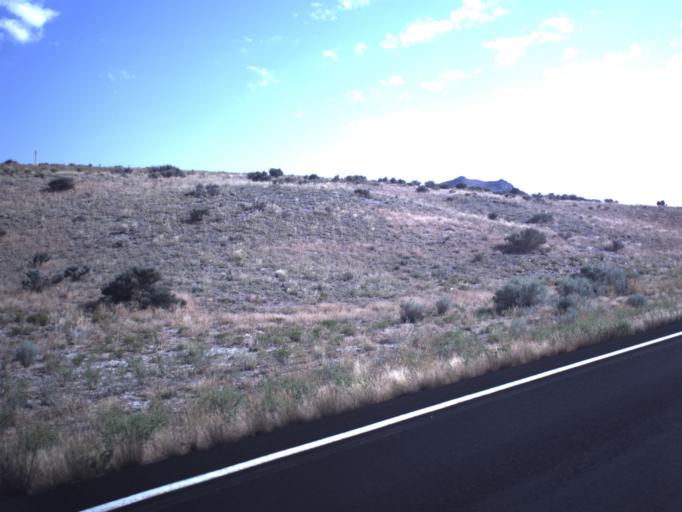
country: US
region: Utah
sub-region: Beaver County
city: Milford
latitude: 38.7910
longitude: -112.9097
